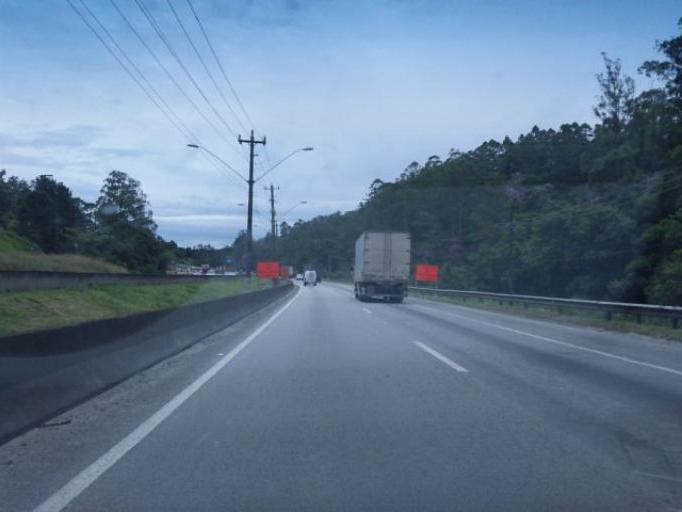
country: BR
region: Sao Paulo
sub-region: Itapecerica Da Serra
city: Itapecerica da Serra
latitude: -23.7717
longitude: -46.9122
